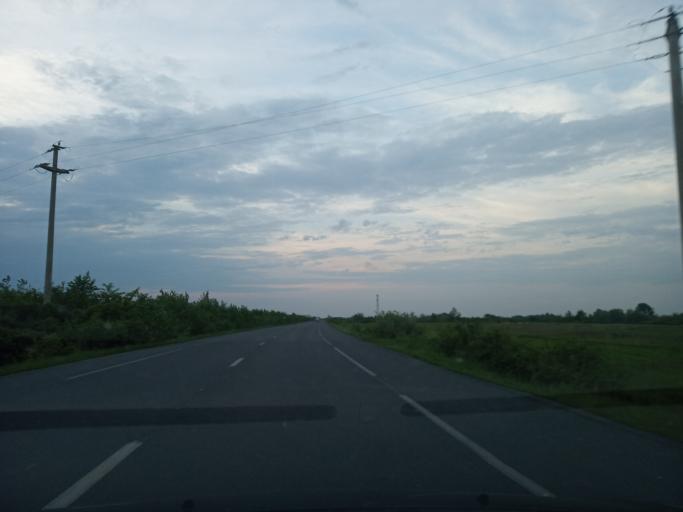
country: RO
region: Timis
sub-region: Oras Deta
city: Deta
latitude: 45.3770
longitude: 21.2331
